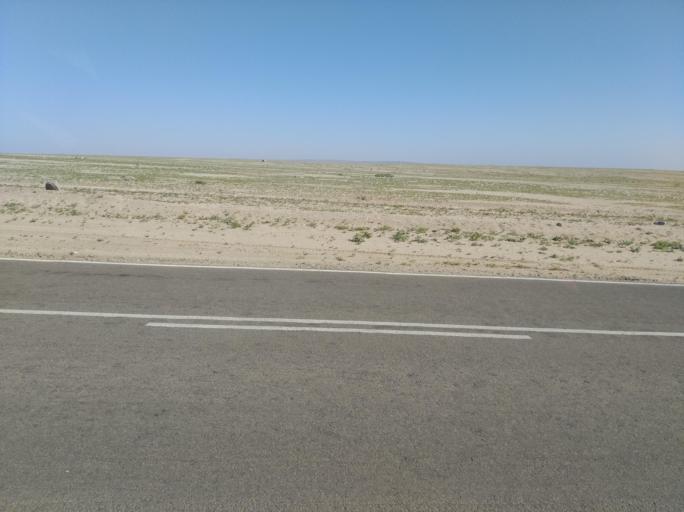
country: CL
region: Atacama
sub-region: Provincia de Copiapo
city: Copiapo
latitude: -27.3162
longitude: -70.8782
